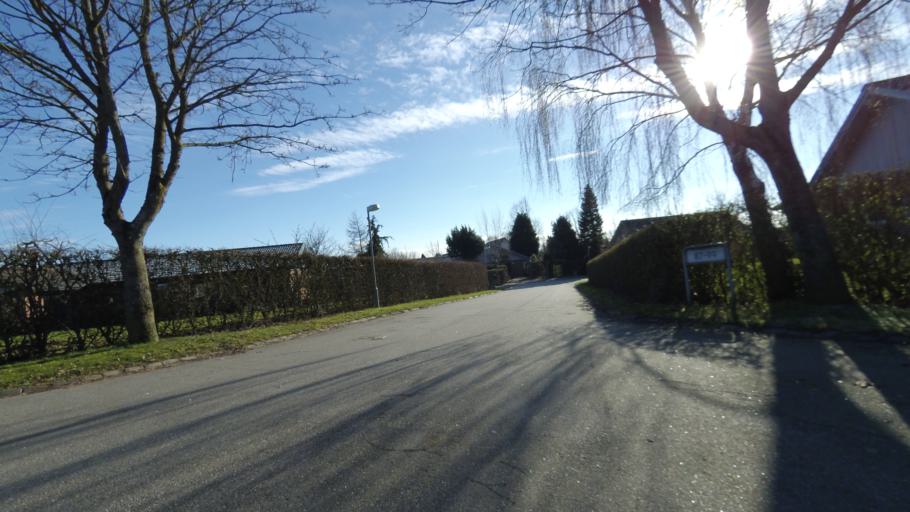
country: DK
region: Central Jutland
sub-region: Arhus Kommune
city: Kolt
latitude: 56.1084
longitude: 10.0643
